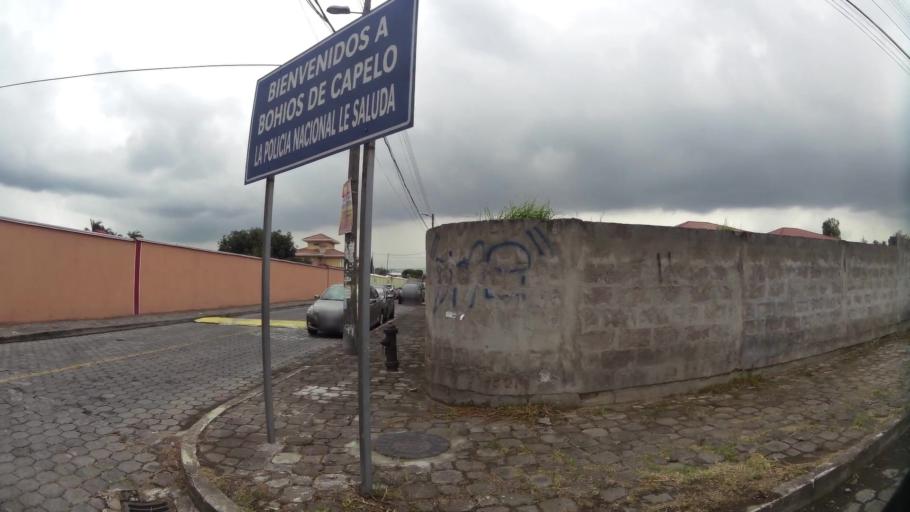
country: EC
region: Pichincha
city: Sangolqui
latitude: -0.3099
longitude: -78.4627
